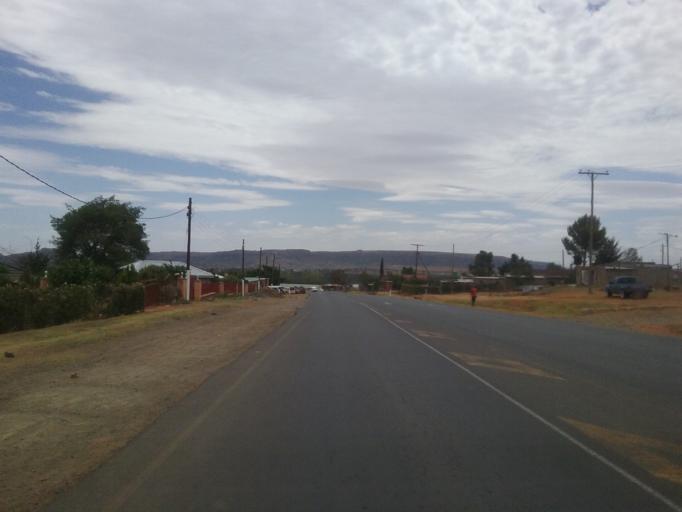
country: LS
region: Maseru
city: Maseru
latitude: -29.4222
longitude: 27.5619
